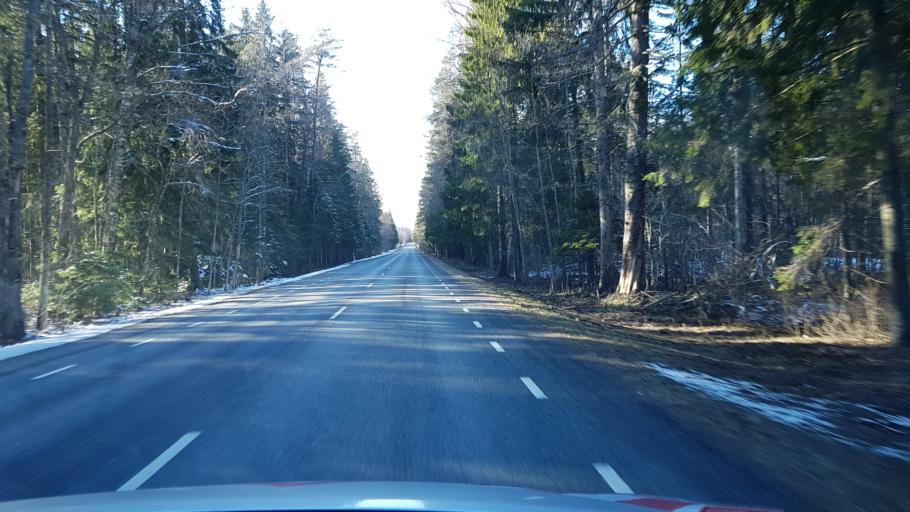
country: EE
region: Laeaene-Virumaa
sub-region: Tapa vald
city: Tapa
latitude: 59.4302
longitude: 25.9743
